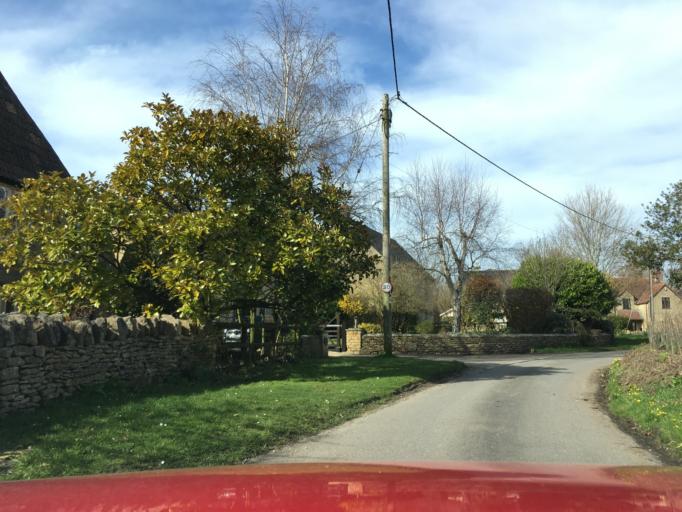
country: GB
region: England
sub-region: Wiltshire
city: Chippenham
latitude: 51.4890
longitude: -2.1182
